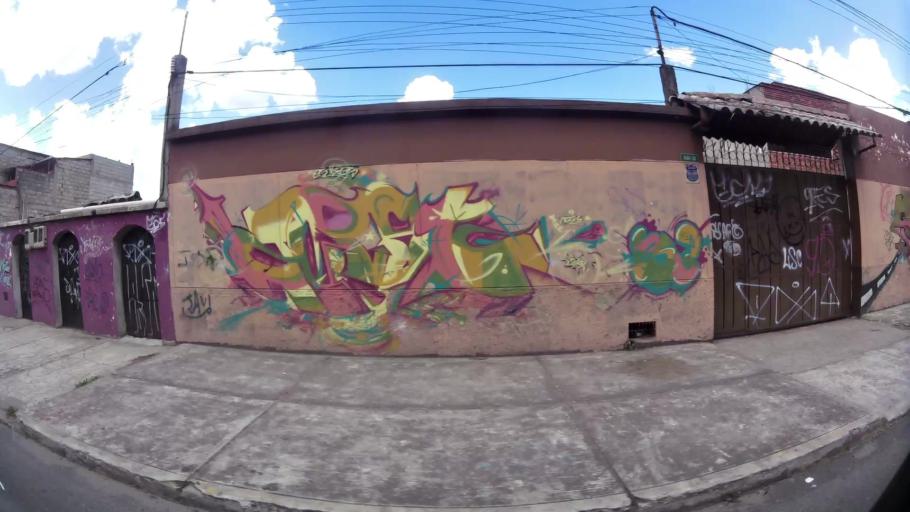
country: EC
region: Pichincha
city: Quito
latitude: -0.1887
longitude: -78.5116
